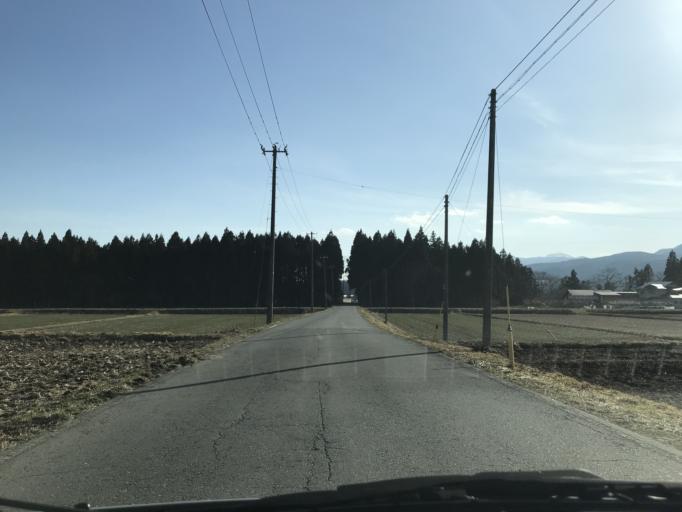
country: JP
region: Iwate
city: Kitakami
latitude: 39.3029
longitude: 141.0059
